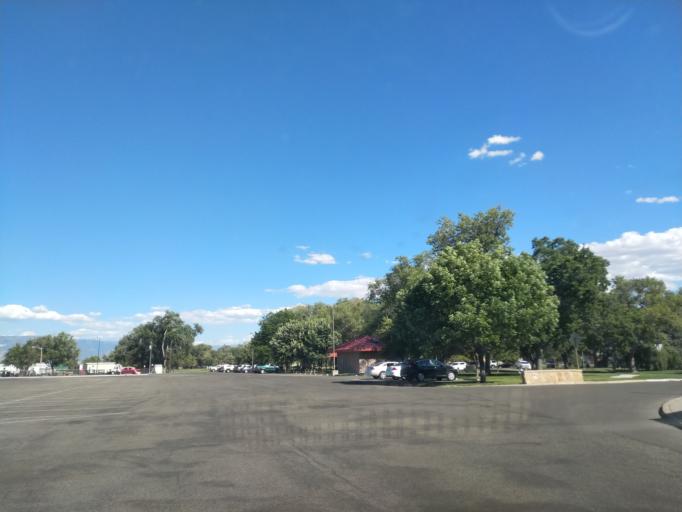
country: US
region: Colorado
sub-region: Mesa County
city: Grand Junction
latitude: 39.0750
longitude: -108.5495
